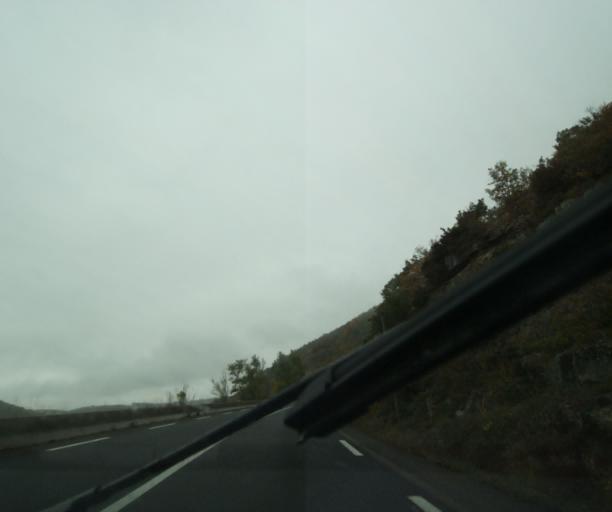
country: FR
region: Midi-Pyrenees
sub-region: Departement de l'Aveyron
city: Millau
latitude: 44.0915
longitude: 3.1249
